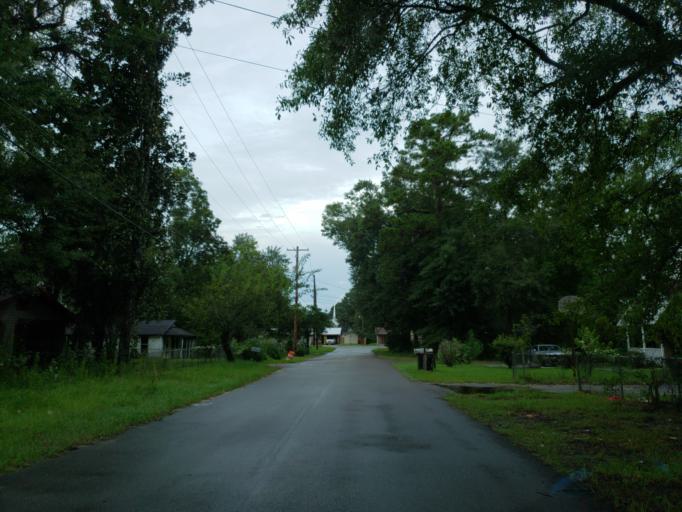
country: US
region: Mississippi
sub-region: Forrest County
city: Hattiesburg
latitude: 31.3091
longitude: -89.2941
